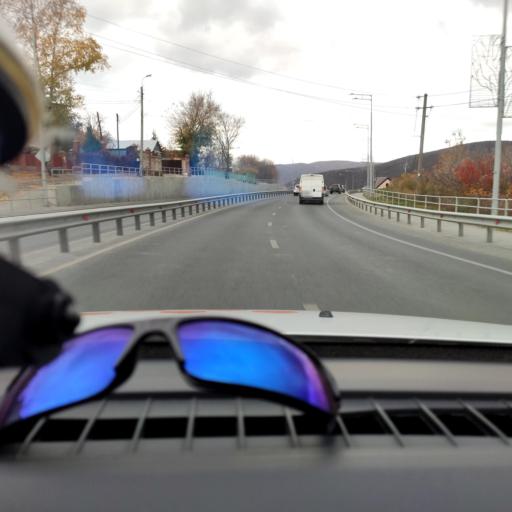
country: RU
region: Samara
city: Volzhskiy
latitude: 53.3667
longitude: 50.1944
